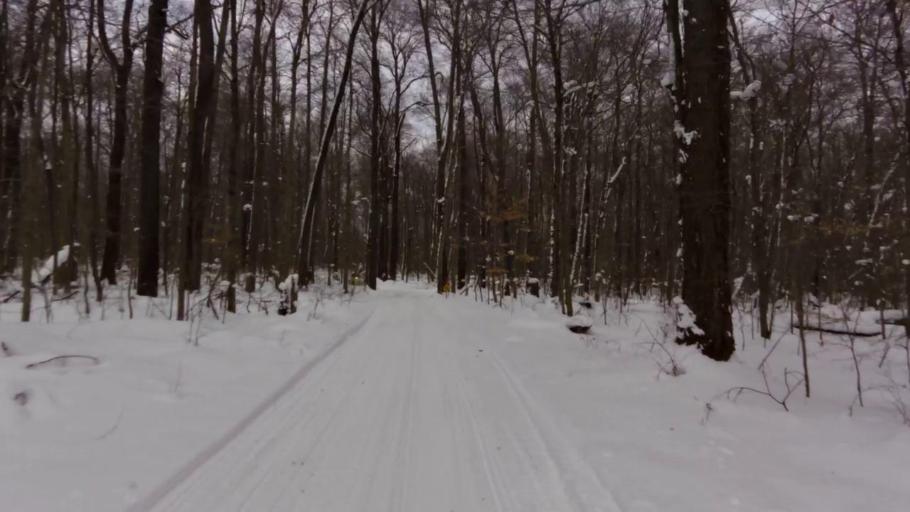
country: US
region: Pennsylvania
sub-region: McKean County
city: Bradford
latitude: 42.0297
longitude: -78.7407
